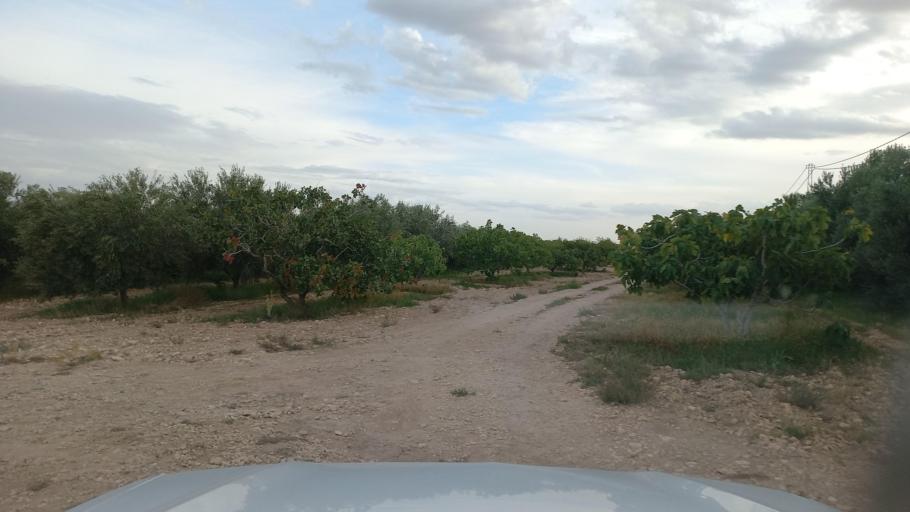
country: TN
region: Al Qasrayn
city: Sbiba
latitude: 35.4400
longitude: 9.0872
